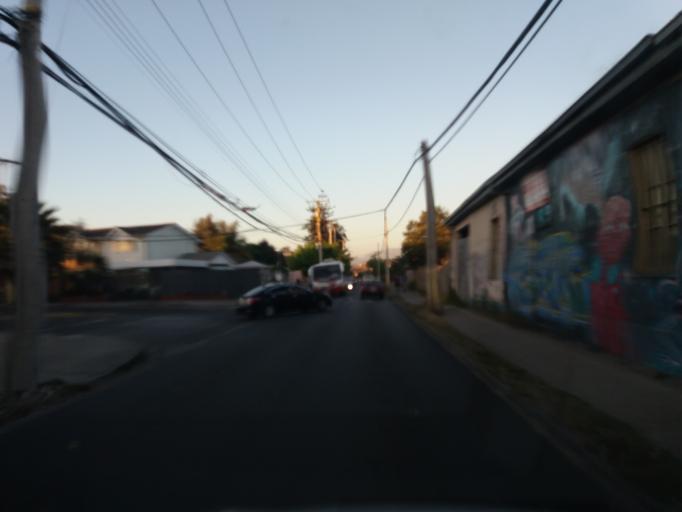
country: CL
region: Valparaiso
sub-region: Provincia de Quillota
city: Quillota
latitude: -32.8899
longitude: -71.2613
